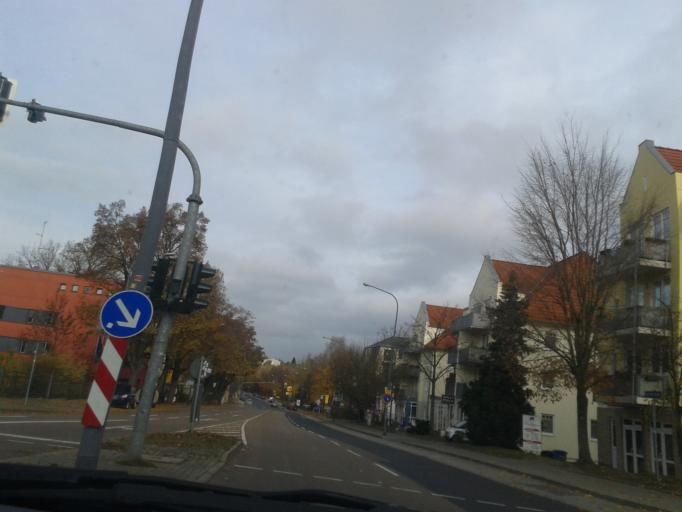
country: DE
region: Saxony
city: Albertstadt
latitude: 51.1105
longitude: 13.7751
